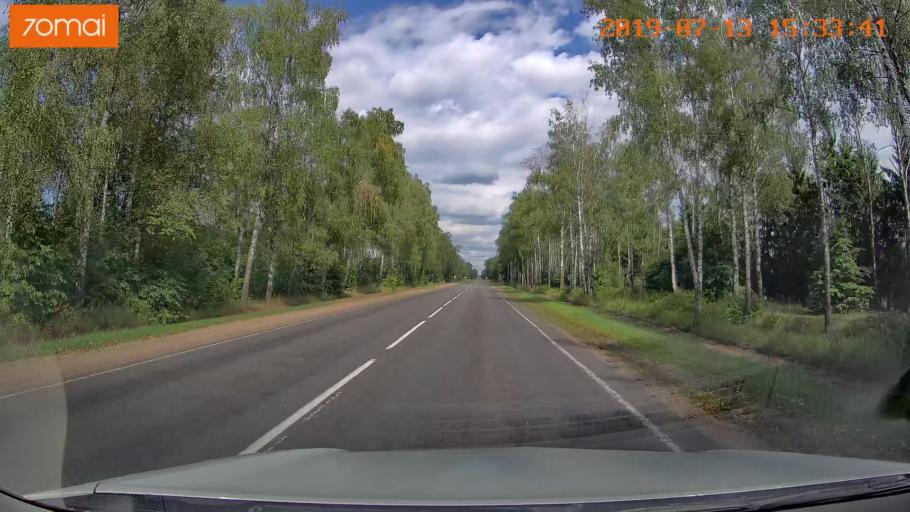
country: BY
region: Mogilev
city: Babruysk
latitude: 53.1191
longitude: 29.1415
